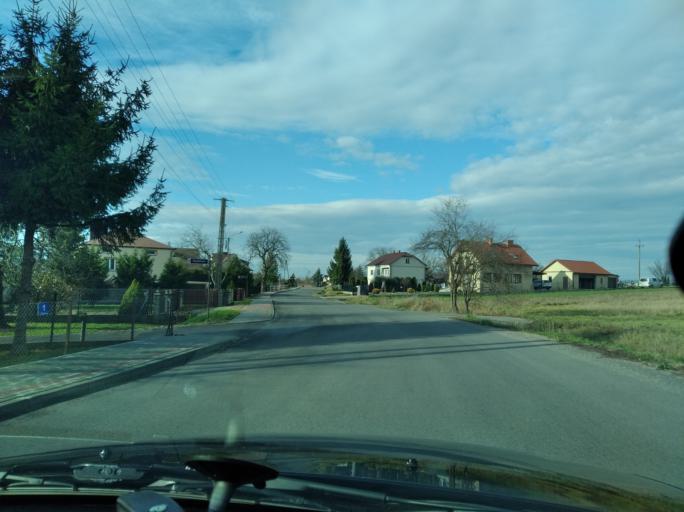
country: PL
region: Subcarpathian Voivodeship
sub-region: Powiat ropczycko-sedziszowski
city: Sedziszow Malopolski
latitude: 50.0836
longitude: 21.7165
